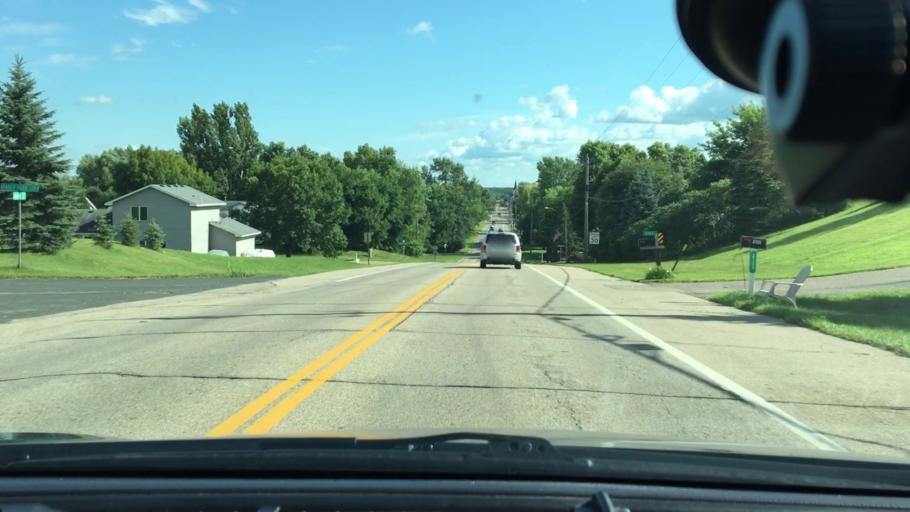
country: US
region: Minnesota
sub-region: Hennepin County
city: Saint Bonifacius
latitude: 44.9109
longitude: -93.7473
